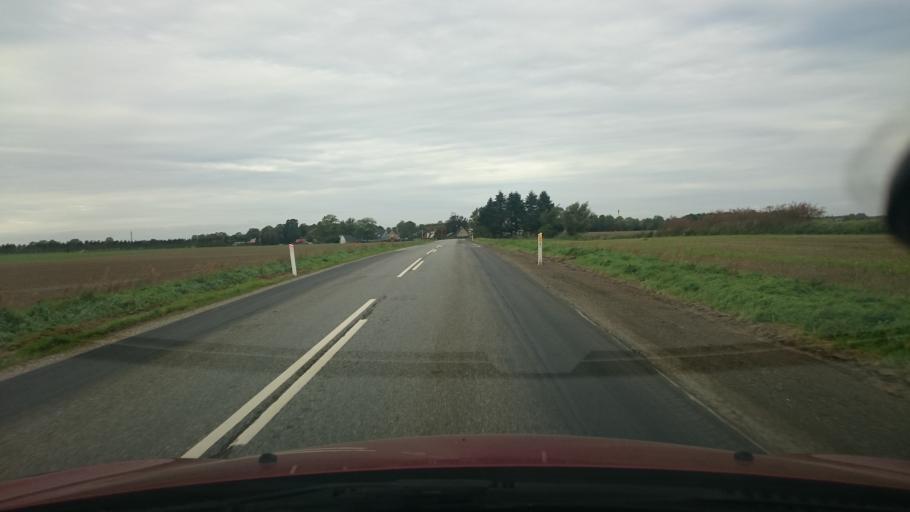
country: DK
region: North Denmark
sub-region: Mariagerfjord Kommune
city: Mariager
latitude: 56.6900
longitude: 9.9848
